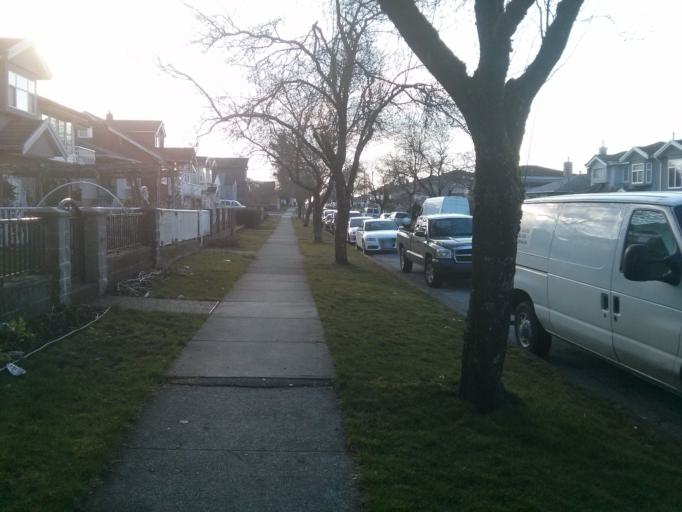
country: CA
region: British Columbia
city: Burnaby
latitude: 49.2477
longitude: -123.0297
